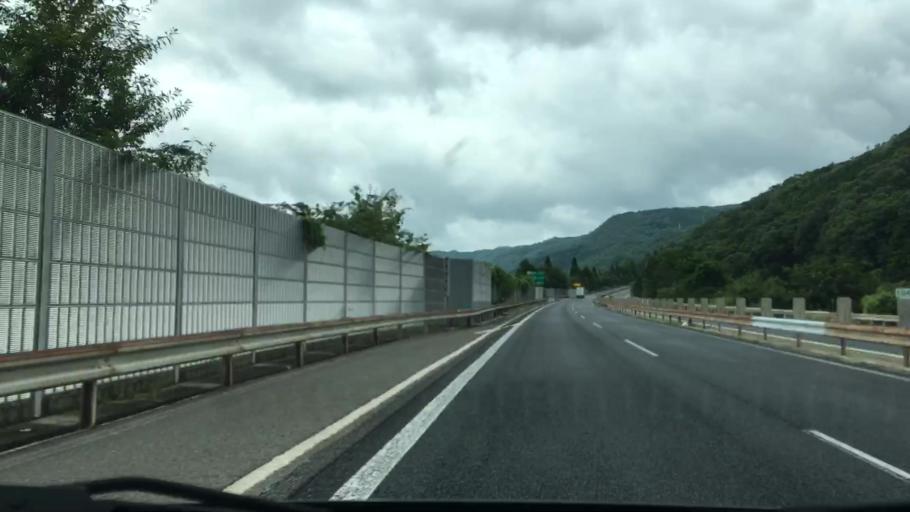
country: JP
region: Okayama
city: Niimi
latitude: 34.9692
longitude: 133.6481
